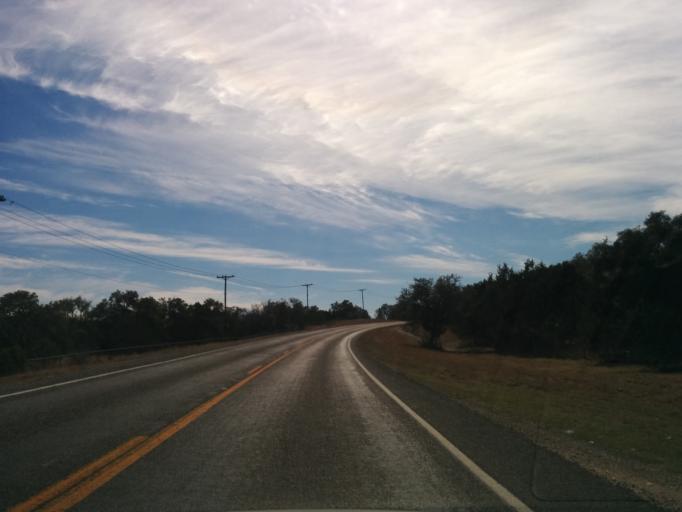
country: US
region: Texas
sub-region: Bexar County
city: Fair Oaks Ranch
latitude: 29.8874
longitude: -98.5568
